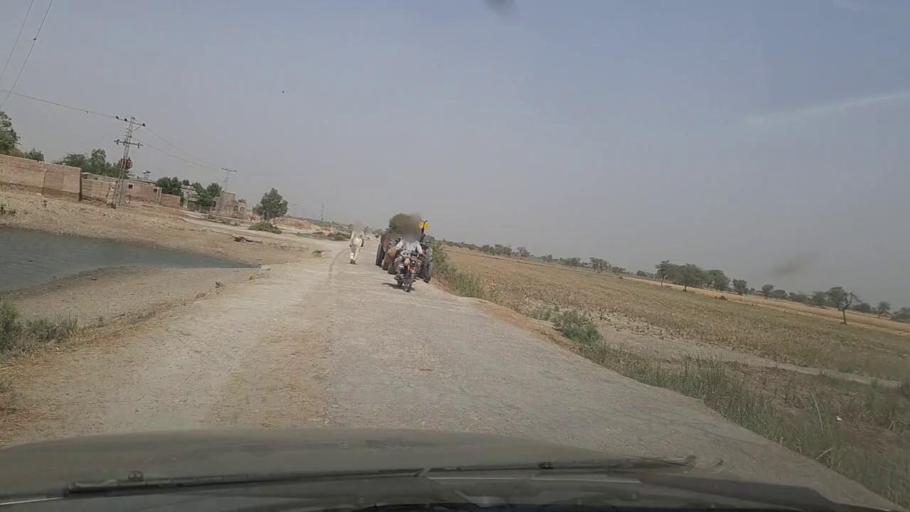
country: PK
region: Balochistan
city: Sohbatpur
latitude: 28.4176
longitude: 68.6848
